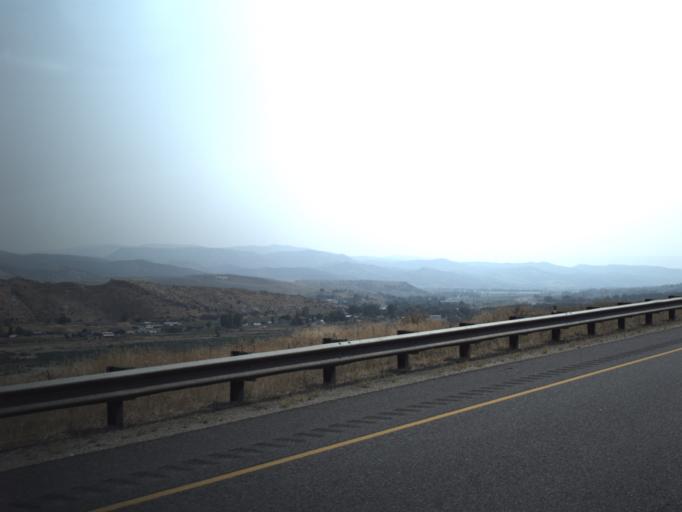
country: US
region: Utah
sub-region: Summit County
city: Coalville
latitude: 40.9340
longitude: -111.4098
